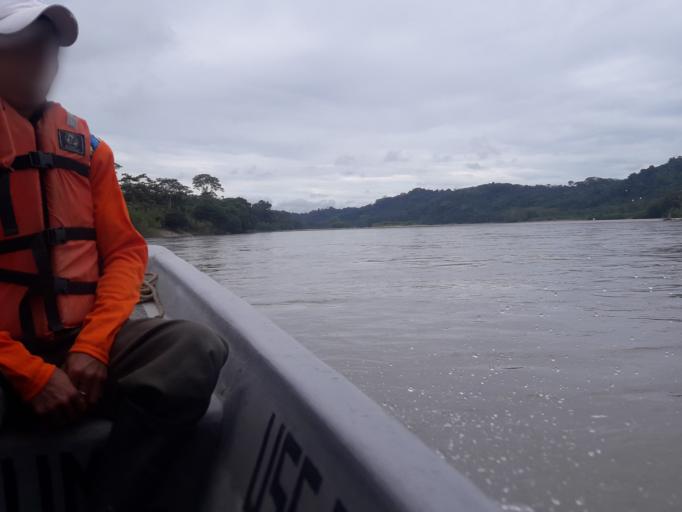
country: EC
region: Orellana
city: Boca Suno
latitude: -0.8790
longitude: -77.2878
